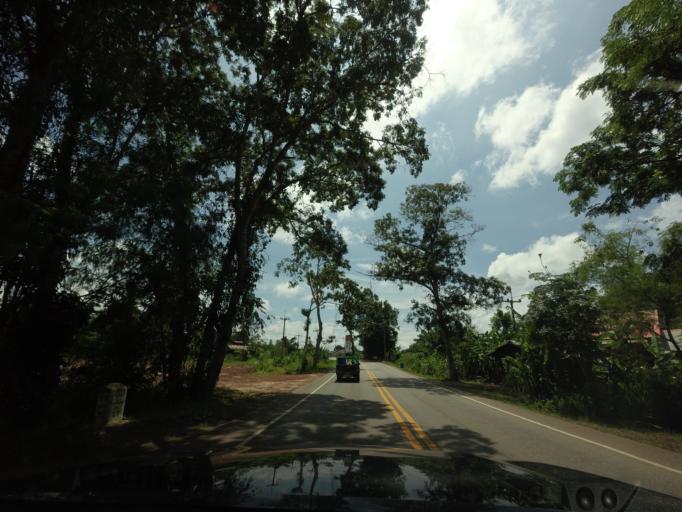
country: TH
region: Nong Khai
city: Pho Tak
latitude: 17.7818
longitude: 102.3773
